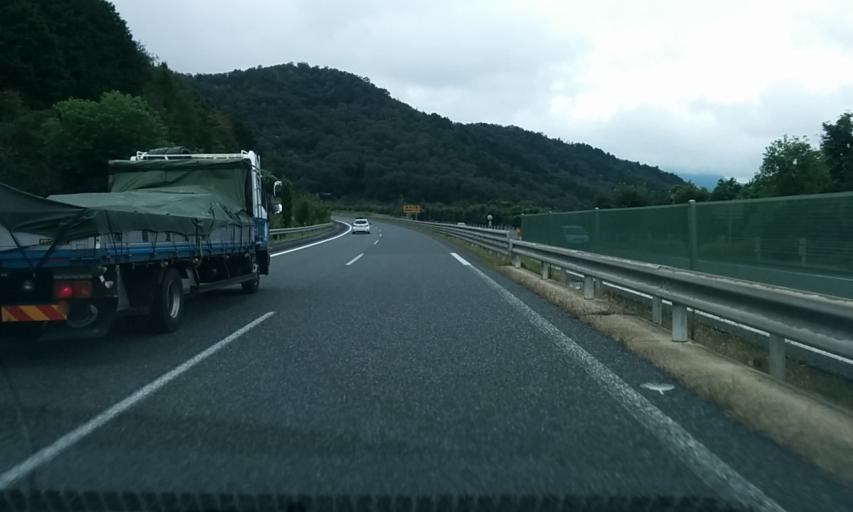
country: JP
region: Kyoto
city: Fukuchiyama
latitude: 35.1924
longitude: 135.1431
